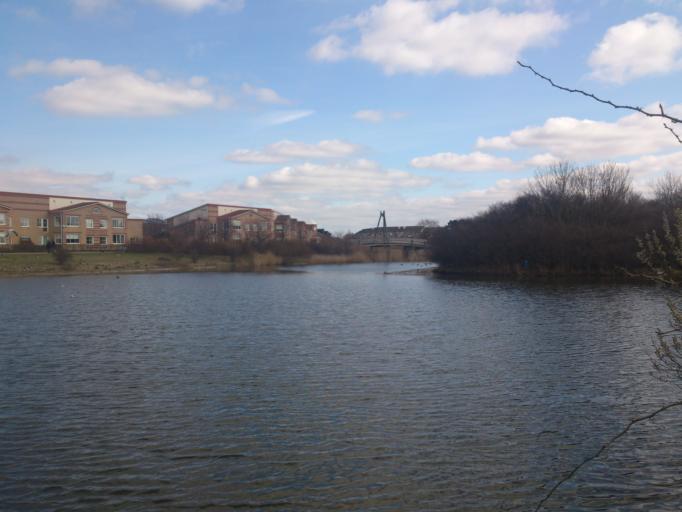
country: SE
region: Skane
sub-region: Lomma Kommun
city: Lomma
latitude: 55.6729
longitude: 13.0605
